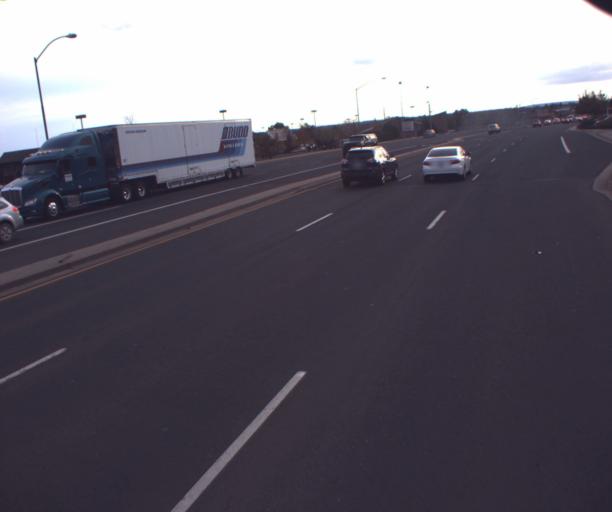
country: US
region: Arizona
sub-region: Coconino County
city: Flagstaff
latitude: 35.2255
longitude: -111.5819
